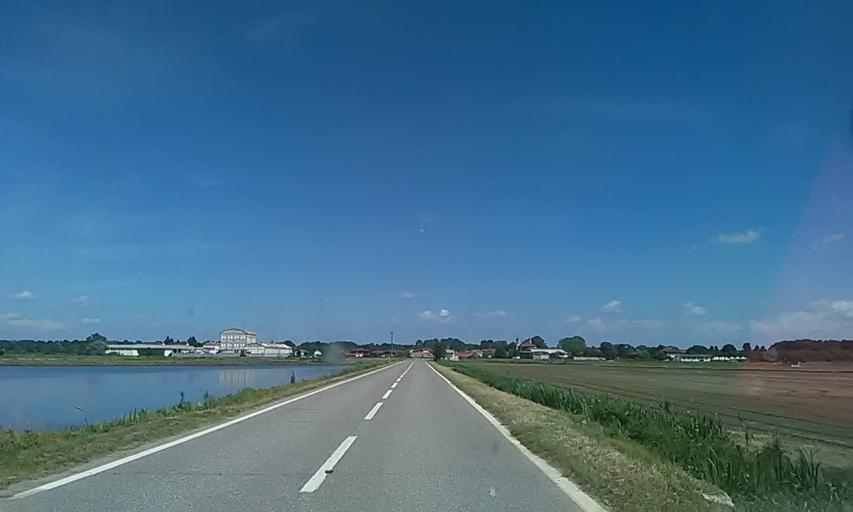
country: IT
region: Piedmont
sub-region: Provincia di Vercelli
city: Albano Vercellese
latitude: 45.4298
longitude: 8.3713
